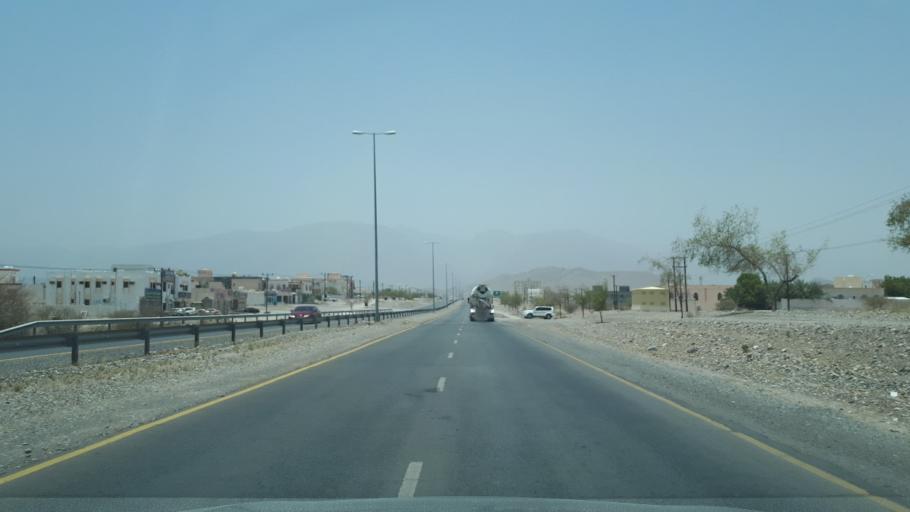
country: OM
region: Al Batinah
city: Rustaq
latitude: 23.4559
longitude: 57.4359
